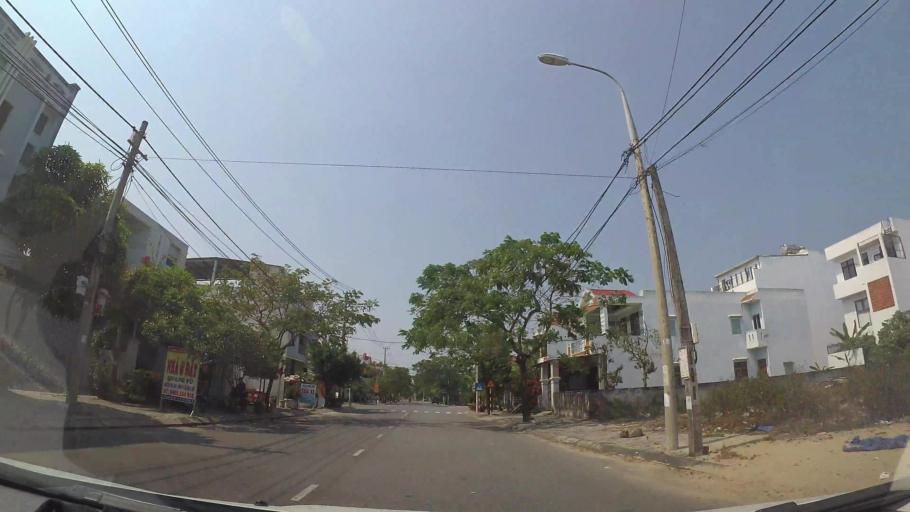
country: VN
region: Da Nang
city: Ngu Hanh Son
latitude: 15.9812
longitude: 108.2737
